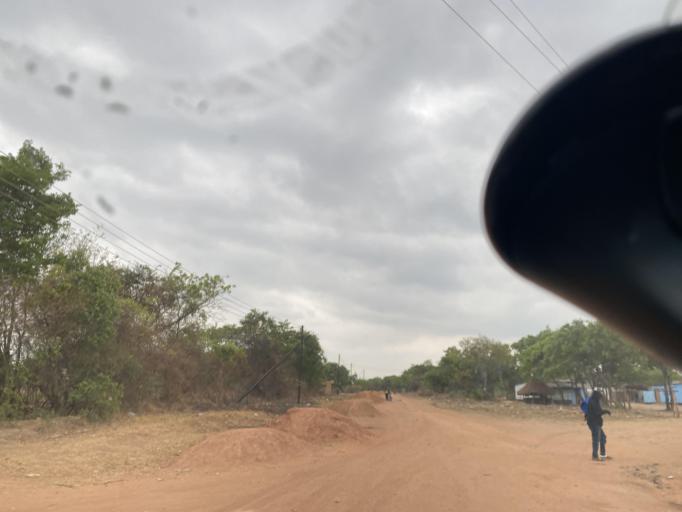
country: ZM
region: Lusaka
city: Chongwe
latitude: -15.2815
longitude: 28.7295
